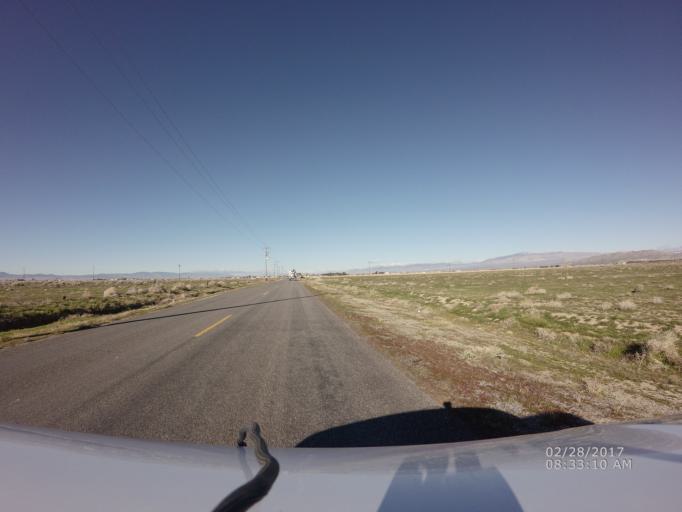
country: US
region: California
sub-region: Kern County
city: Rosamond
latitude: 34.8202
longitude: -118.2353
